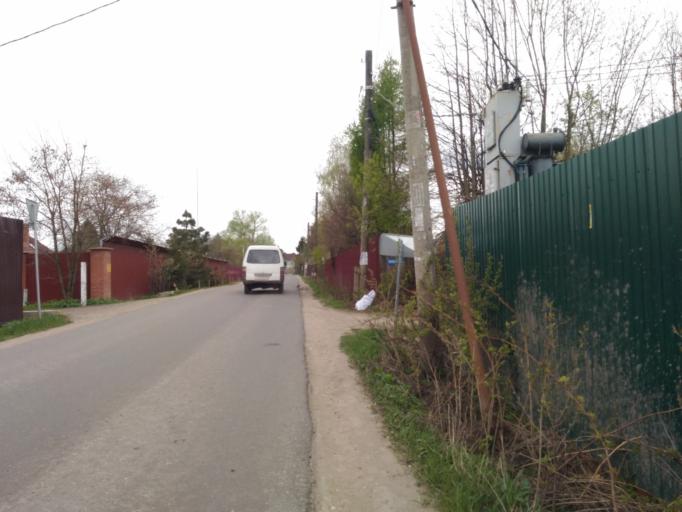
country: RU
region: Moskovskaya
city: Dedovsk
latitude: 55.8519
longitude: 37.1420
